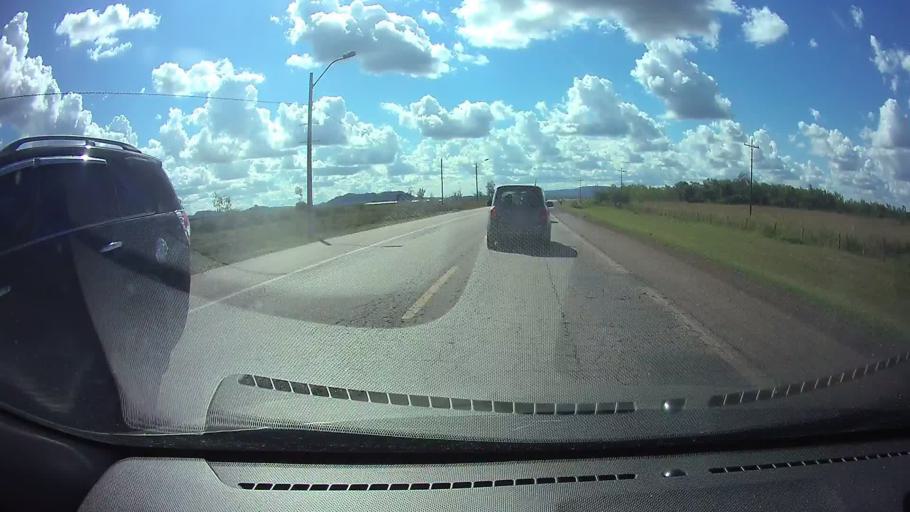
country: PY
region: Paraguari
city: Sapucai
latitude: -25.7456
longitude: -56.8046
